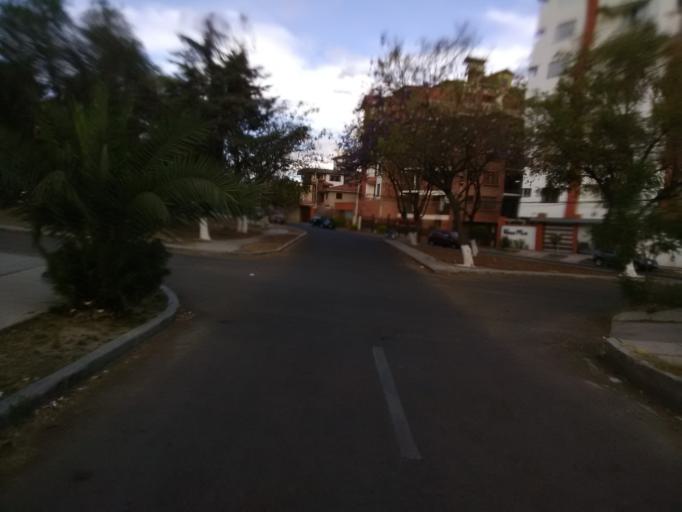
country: BO
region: Cochabamba
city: Cochabamba
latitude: -17.3668
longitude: -66.1724
